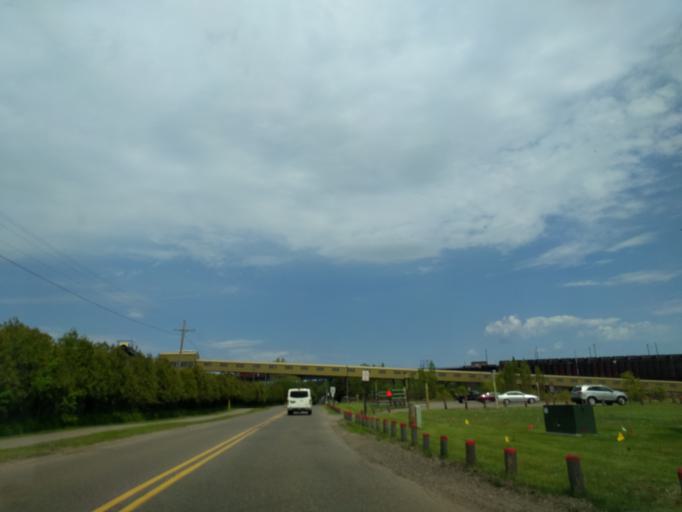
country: US
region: Michigan
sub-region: Marquette County
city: Marquette
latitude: 46.5781
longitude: -87.3924
